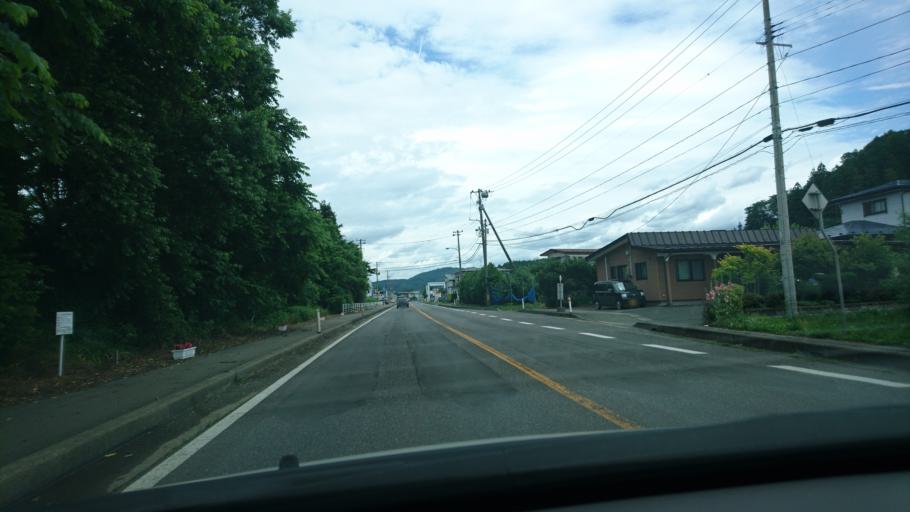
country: JP
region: Iwate
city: Morioka-shi
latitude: 39.6258
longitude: 141.1833
